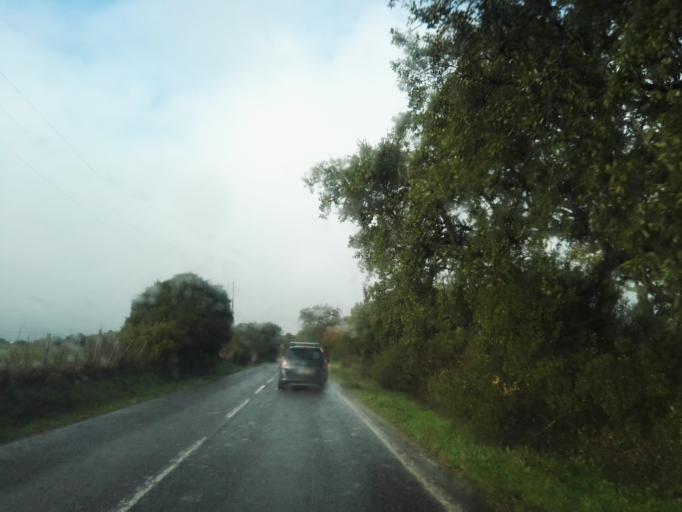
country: PT
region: Santarem
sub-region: Cartaxo
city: Cartaxo
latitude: 39.2205
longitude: -8.7900
